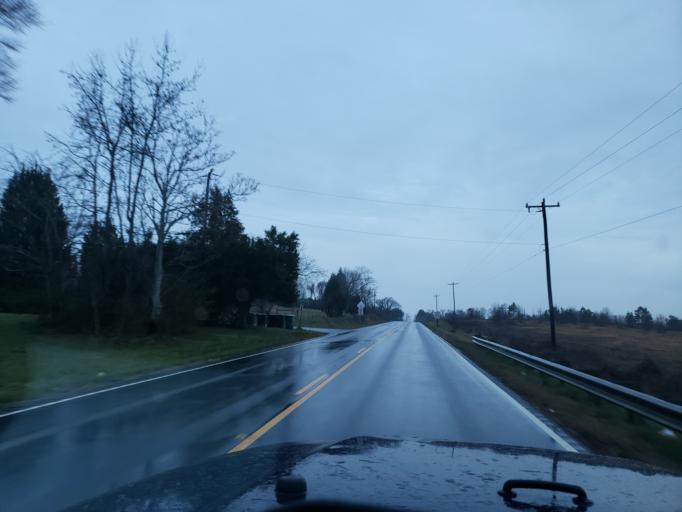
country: US
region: South Carolina
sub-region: Cherokee County
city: Blacksburg
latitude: 35.1556
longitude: -81.4511
